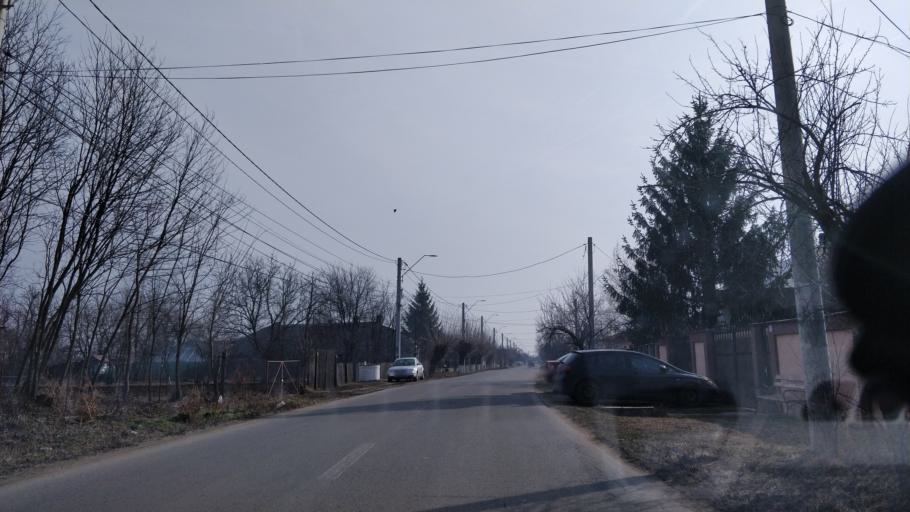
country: RO
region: Giurgiu
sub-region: Comuna Ulmi
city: Ulmi
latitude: 44.4638
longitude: 25.7764
